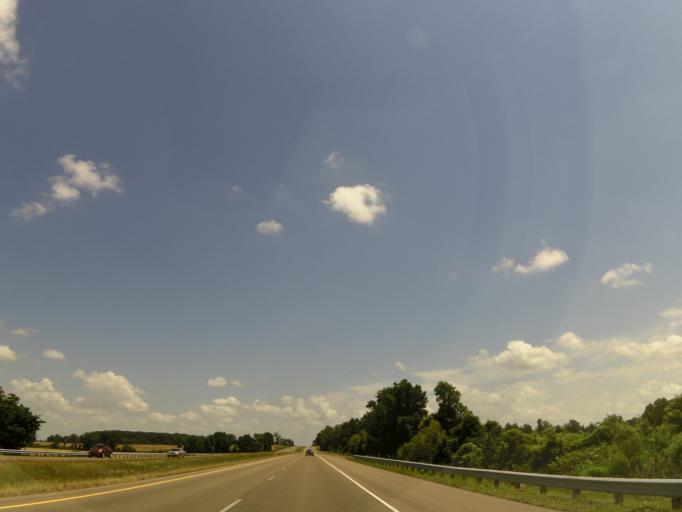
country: US
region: Tennessee
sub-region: Crockett County
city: Alamo
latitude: 35.8780
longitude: -89.2230
